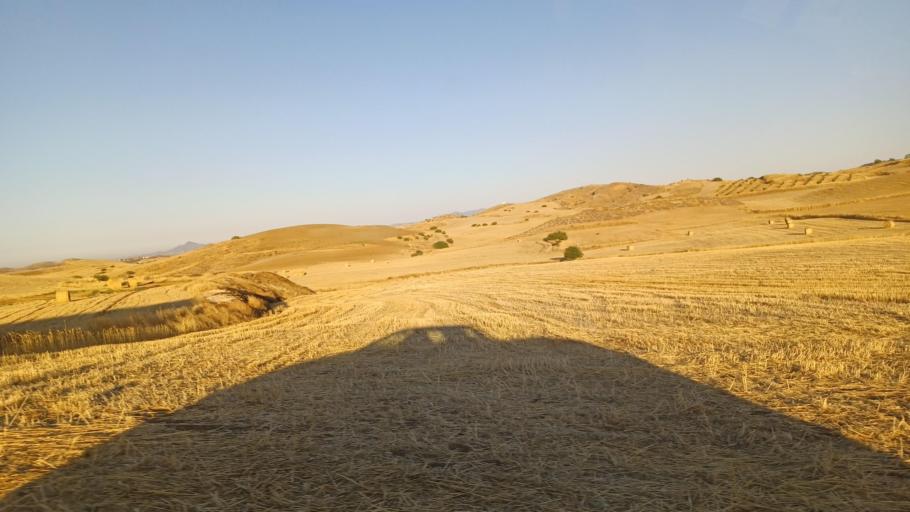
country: CY
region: Larnaka
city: Troulloi
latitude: 35.0292
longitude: 33.6390
